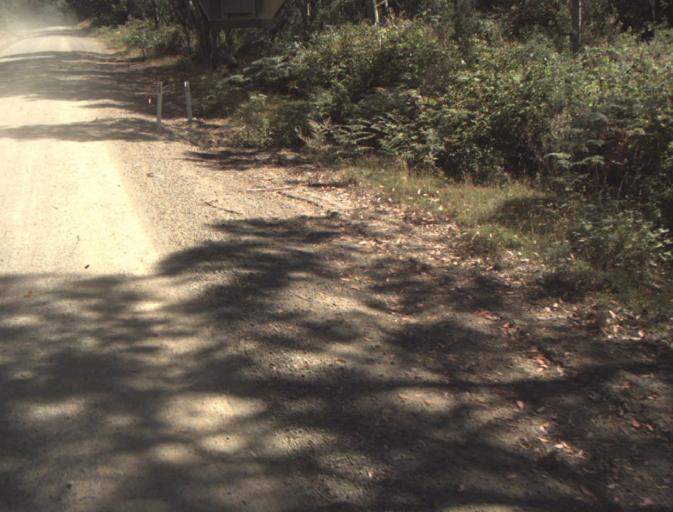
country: AU
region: Tasmania
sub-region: Dorset
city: Scottsdale
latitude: -41.3374
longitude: 147.4331
